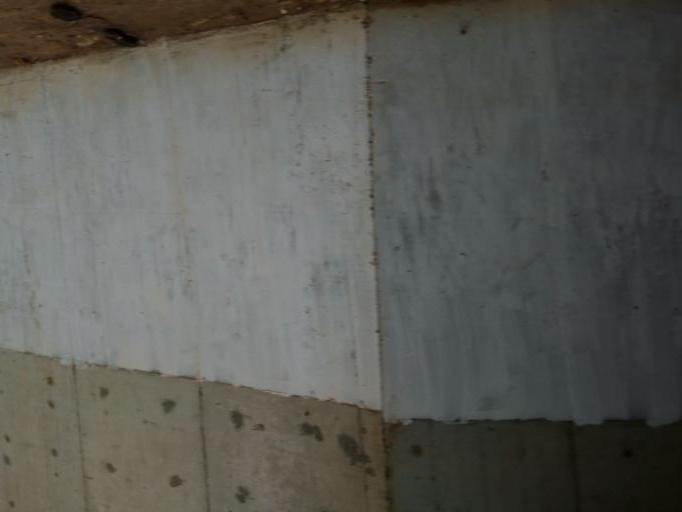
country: DZ
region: Tipaza
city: Tipasa
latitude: 36.5768
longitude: 2.5459
